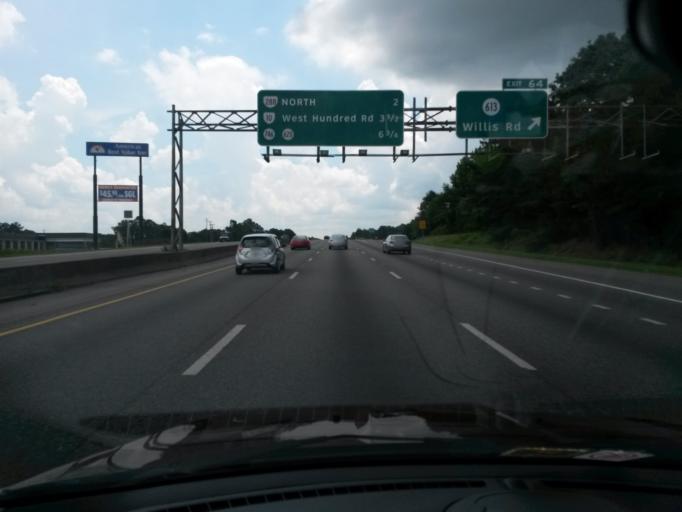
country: US
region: Virginia
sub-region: Chesterfield County
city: Bellwood
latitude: 37.4043
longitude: -77.4253
